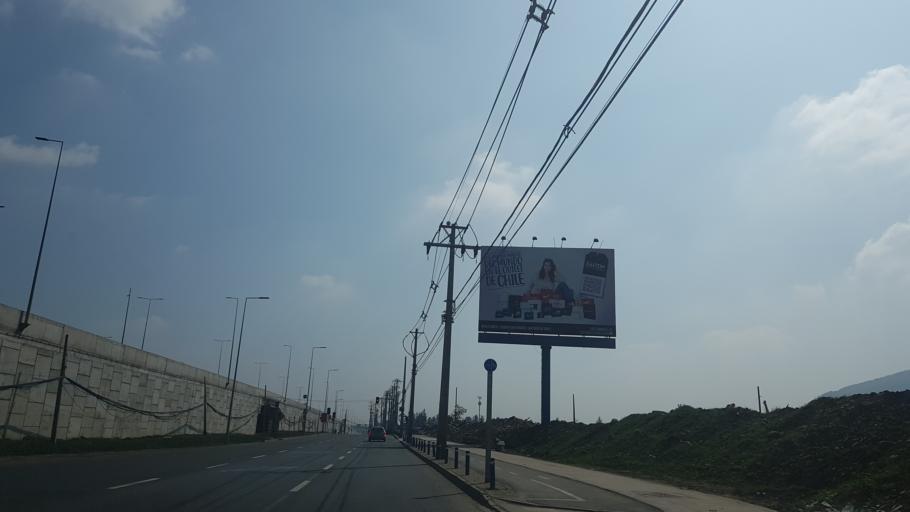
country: CL
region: Santiago Metropolitan
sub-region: Provincia de Chacabuco
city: Chicureo Abajo
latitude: -33.3488
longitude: -70.7076
